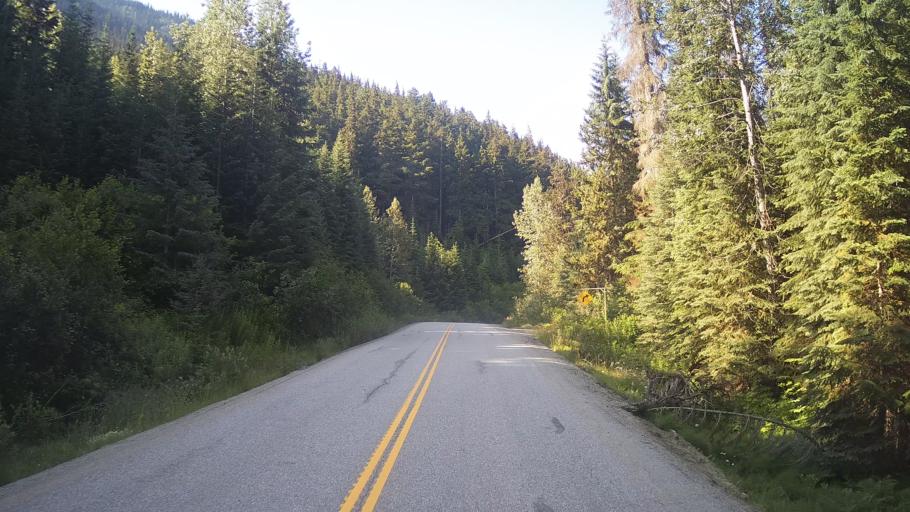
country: CA
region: British Columbia
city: Lillooet
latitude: 50.4226
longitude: -122.2736
